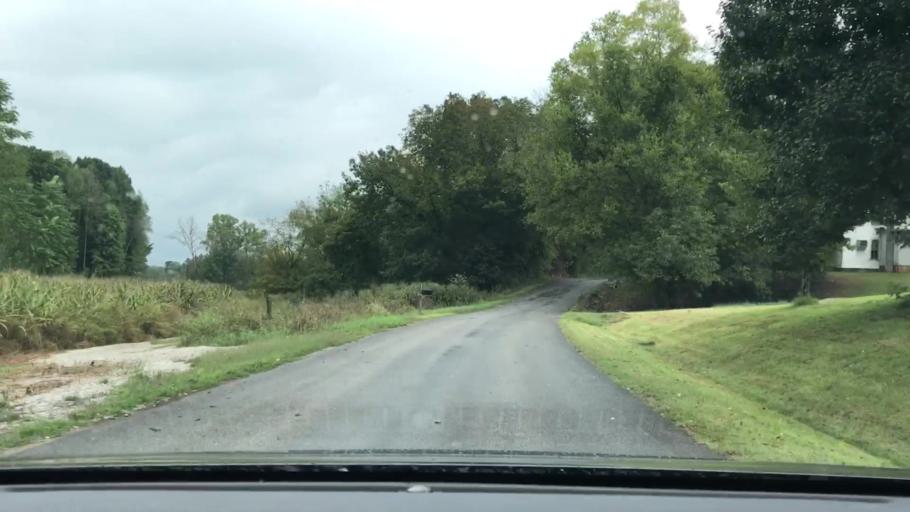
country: US
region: Tennessee
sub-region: Macon County
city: Red Boiling Springs
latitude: 36.5925
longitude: -85.7774
